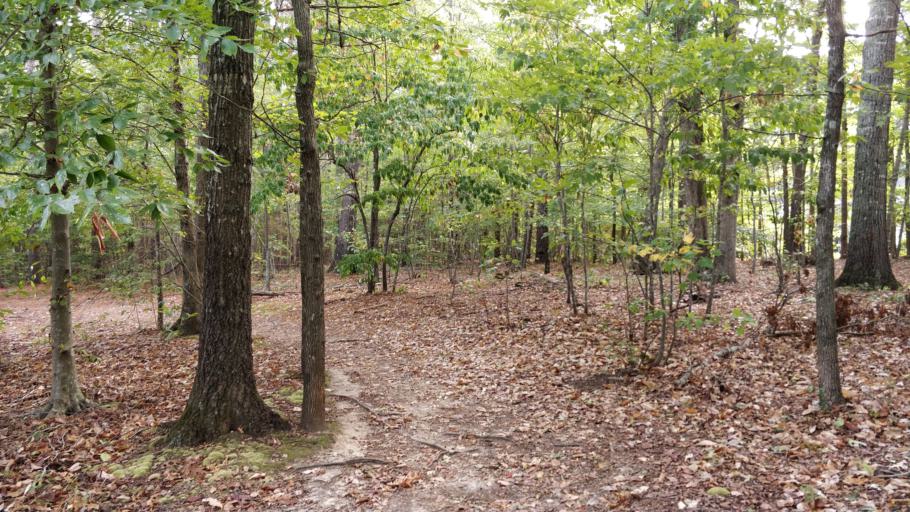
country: US
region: North Carolina
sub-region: Wake County
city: West Raleigh
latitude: 35.9059
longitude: -78.6673
